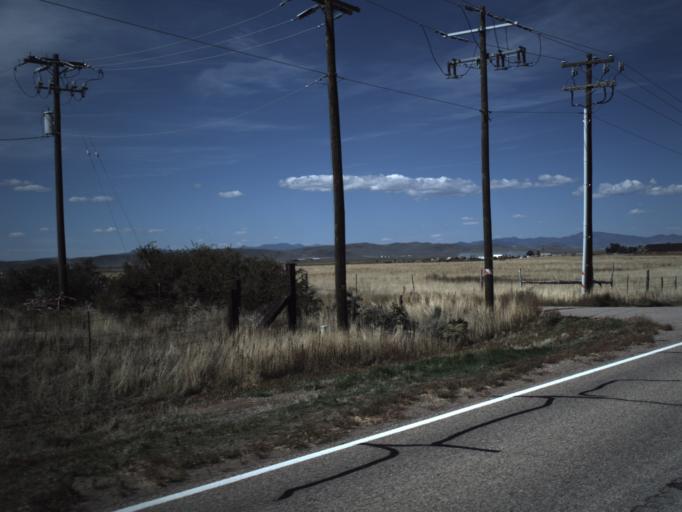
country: US
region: Utah
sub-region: Washington County
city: Enterprise
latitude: 37.6119
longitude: -113.6612
